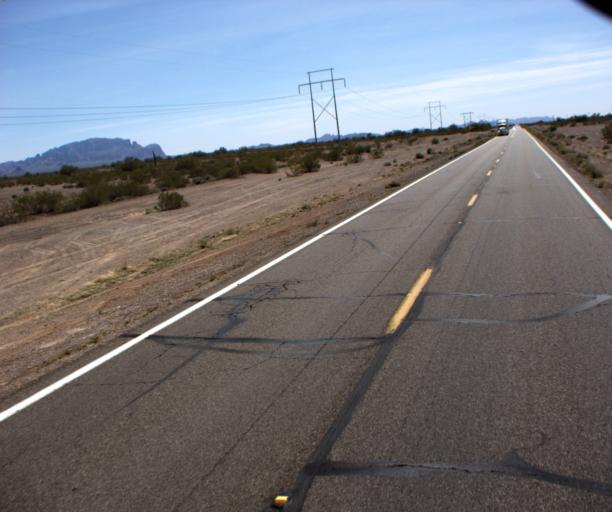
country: US
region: Arizona
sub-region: La Paz County
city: Quartzsite
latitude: 33.5035
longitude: -114.2170
